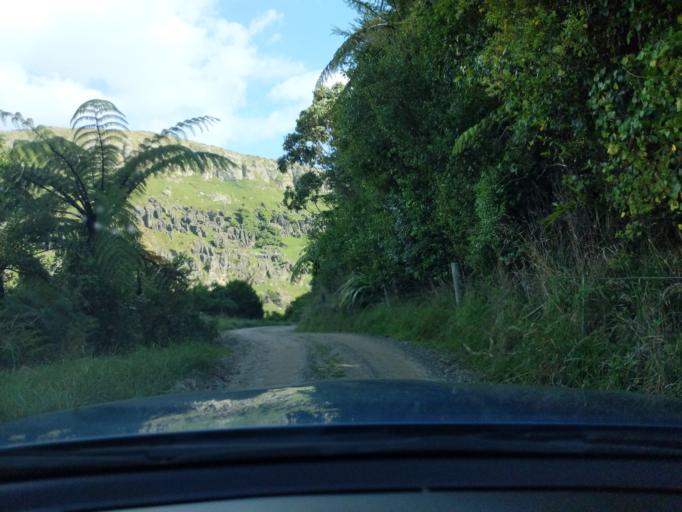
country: NZ
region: Tasman
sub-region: Tasman District
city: Takaka
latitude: -40.6446
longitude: 172.4319
